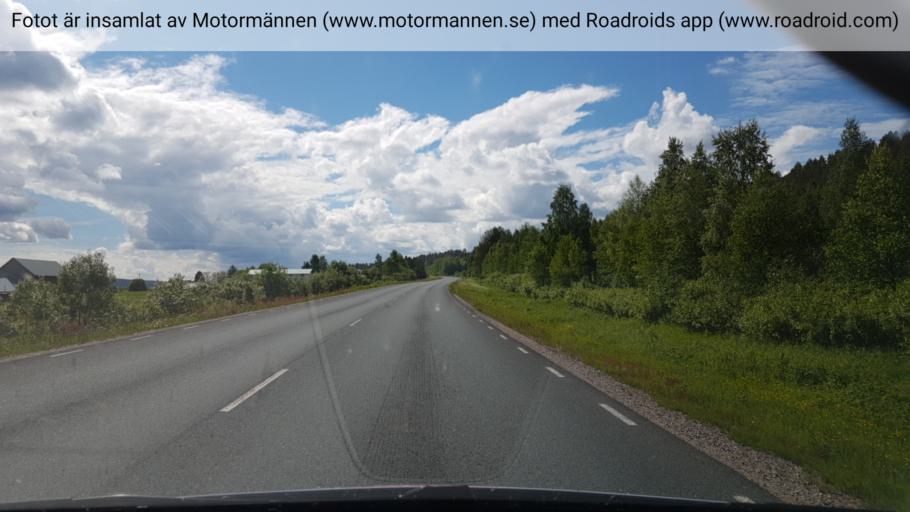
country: SE
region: Norrbotten
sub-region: Overtornea Kommun
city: OEvertornea
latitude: 66.3611
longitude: 23.6497
